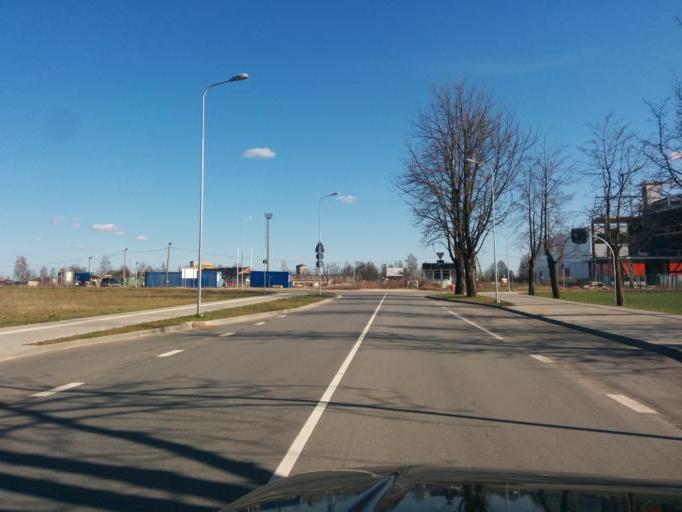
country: LV
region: Jelgava
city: Jelgava
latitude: 56.6519
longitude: 23.7497
